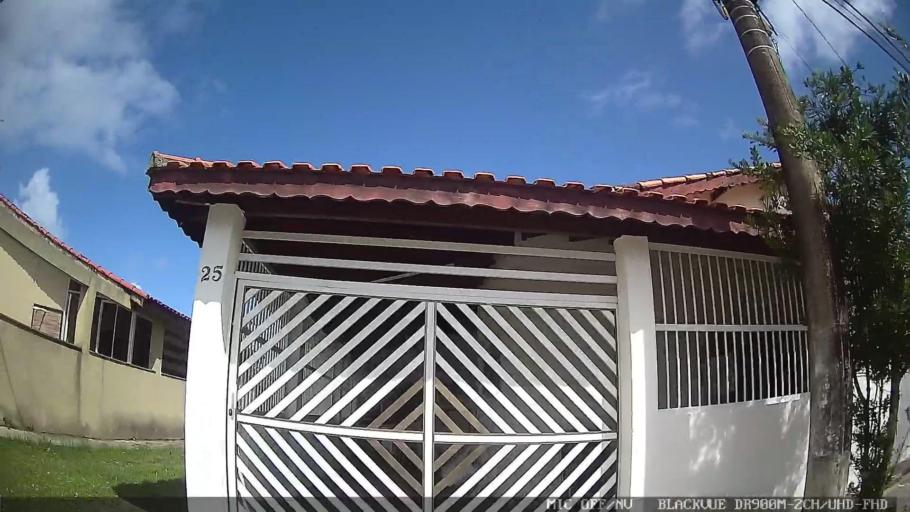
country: BR
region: Sao Paulo
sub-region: Itanhaem
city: Itanhaem
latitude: -24.2279
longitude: -46.8656
